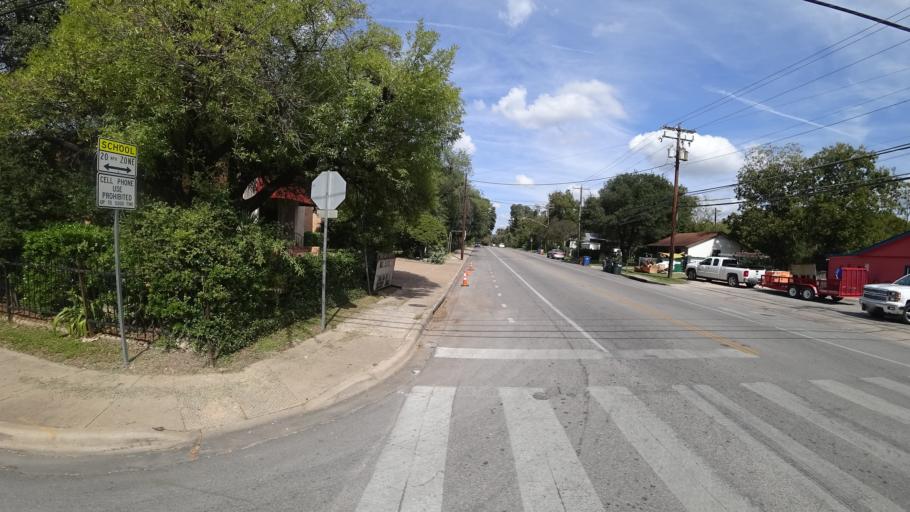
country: US
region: Texas
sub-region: Travis County
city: Austin
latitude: 30.2625
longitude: -97.7039
